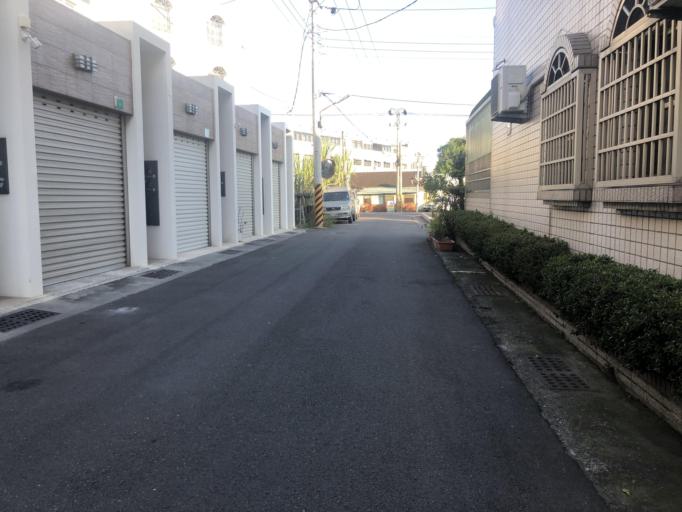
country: TW
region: Taiwan
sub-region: Tainan
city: Tainan
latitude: 23.0382
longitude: 120.1841
